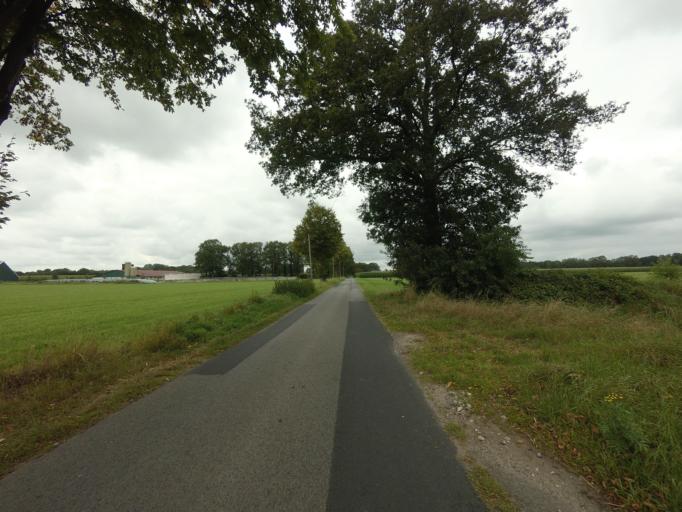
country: NL
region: Overijssel
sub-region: Gemeente Losser
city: Losser
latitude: 52.2573
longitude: 7.0716
